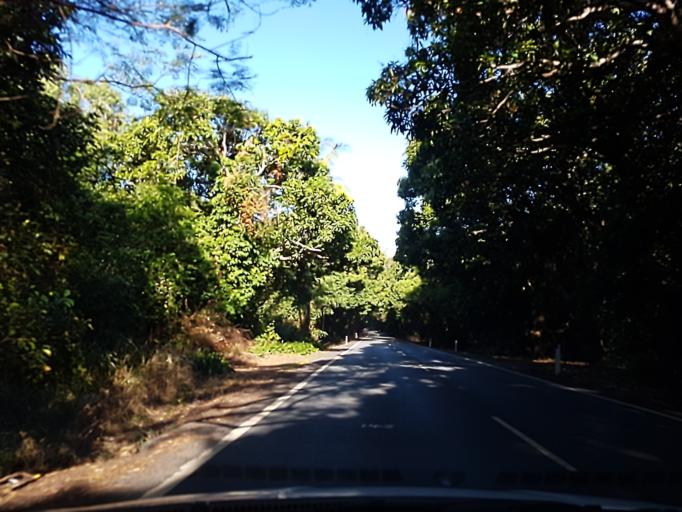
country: AU
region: Queensland
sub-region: Cairns
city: Palm Cove
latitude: -16.7271
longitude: 145.6472
